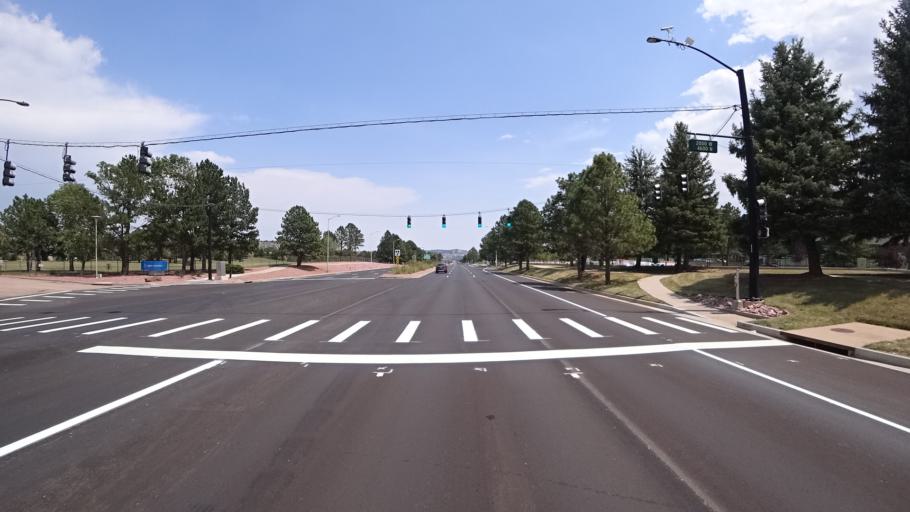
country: US
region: Colorado
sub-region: El Paso County
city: Manitou Springs
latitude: 38.8966
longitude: -104.8665
